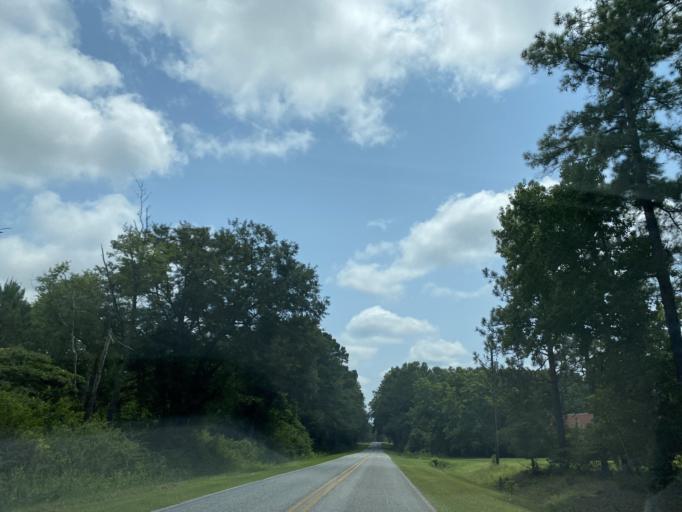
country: US
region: Georgia
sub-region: Telfair County
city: Lumber City
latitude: 31.9927
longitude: -82.7045
